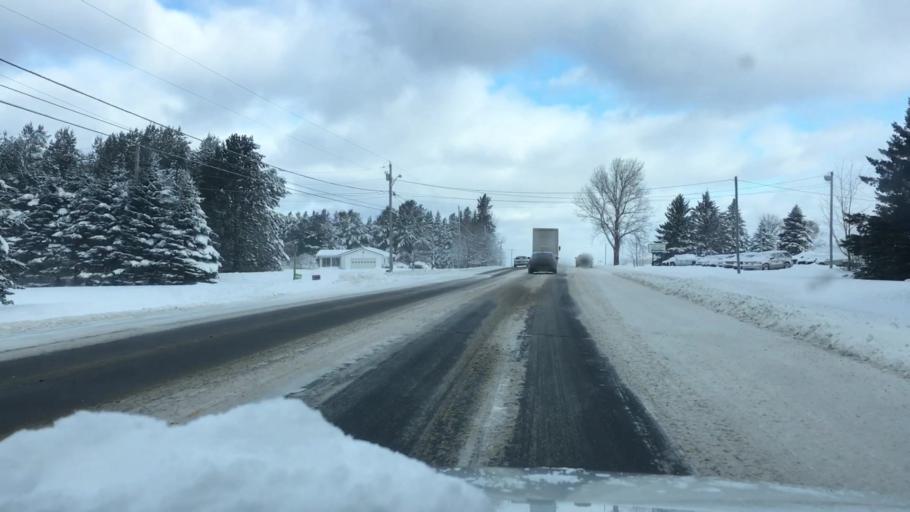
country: US
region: Maine
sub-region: Aroostook County
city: Caribou
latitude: 46.7918
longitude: -67.9912
